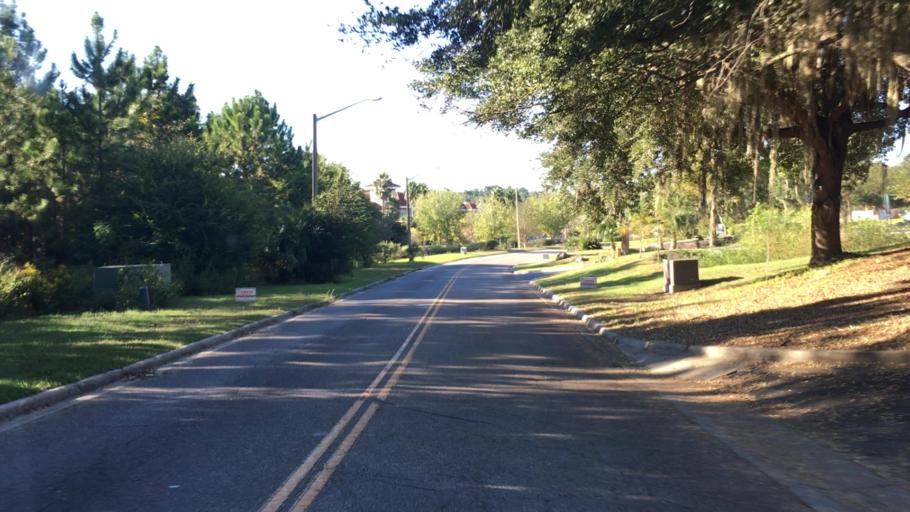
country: US
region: Florida
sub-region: Alachua County
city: Alachua
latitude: 29.6905
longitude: -82.4506
